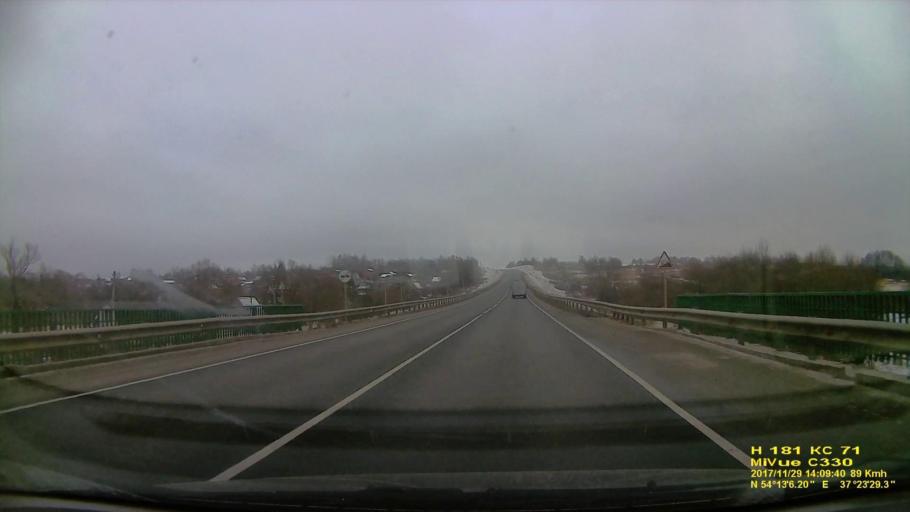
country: RU
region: Tula
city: Leninskiy
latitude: 54.2182
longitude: 37.3916
